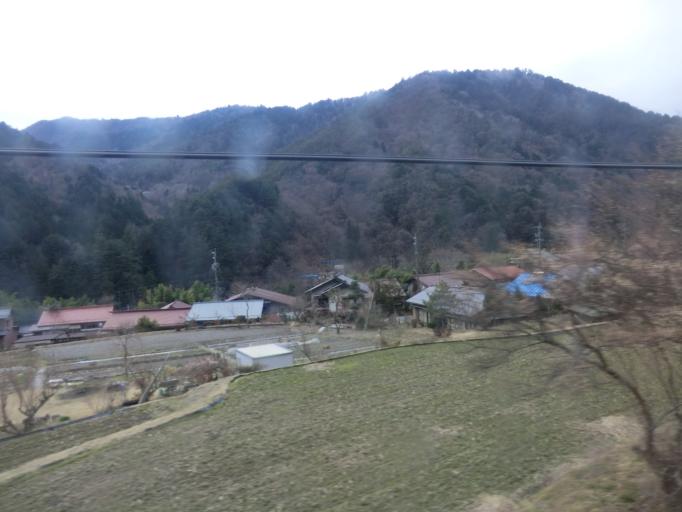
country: JP
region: Nagano
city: Ina
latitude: 35.7545
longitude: 137.7104
